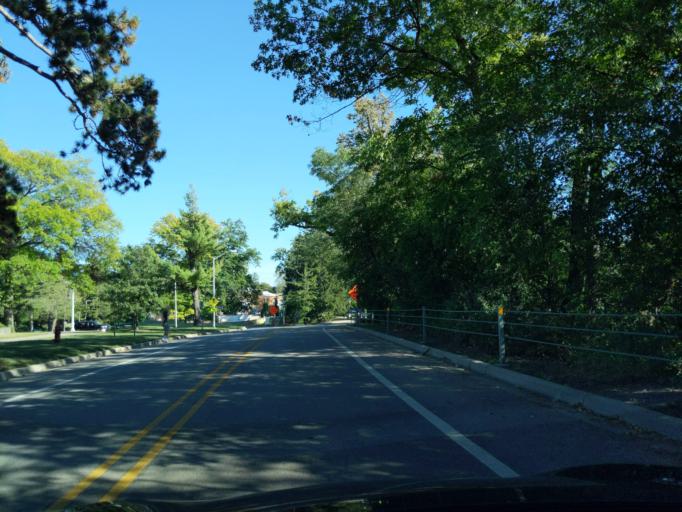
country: US
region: Michigan
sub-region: Ingham County
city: East Lansing
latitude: 42.7335
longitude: -84.4880
